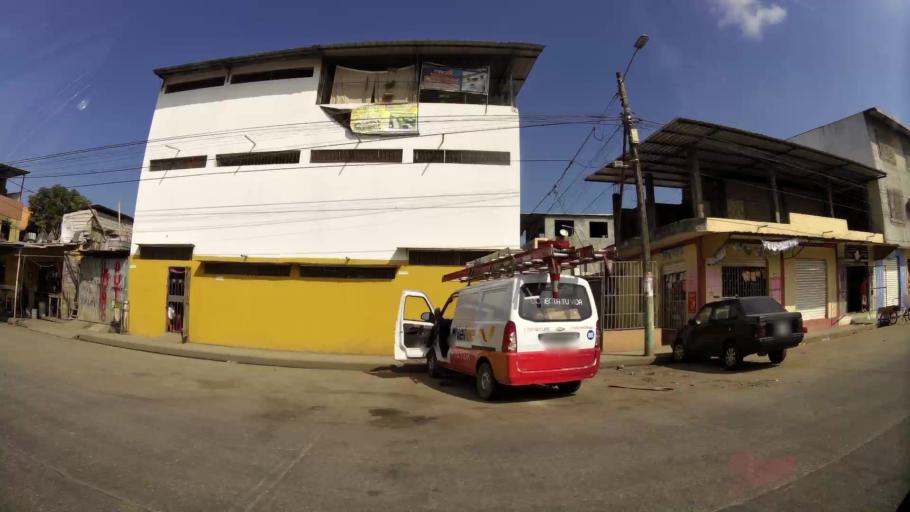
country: EC
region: Guayas
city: Eloy Alfaro
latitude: -2.1668
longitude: -79.7977
